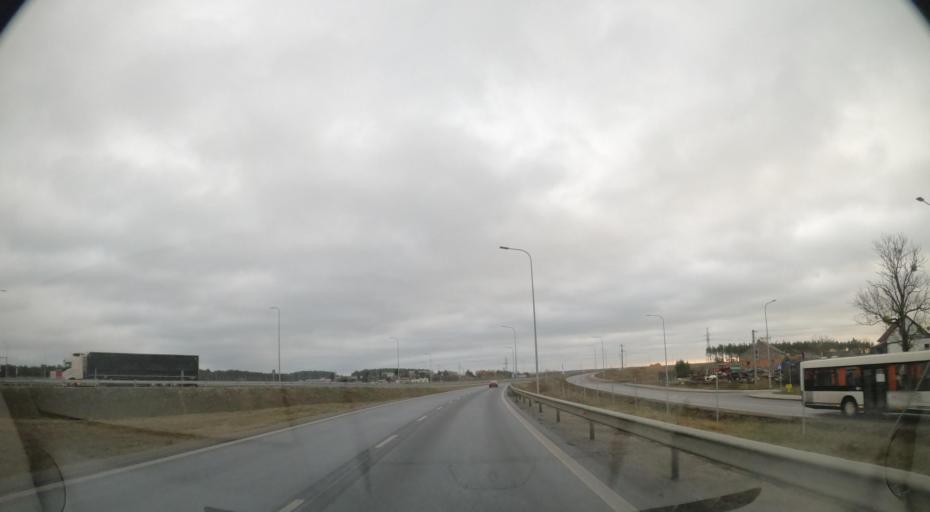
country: PL
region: Kujawsko-Pomorskie
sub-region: Powiat bydgoski
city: Biale Blota
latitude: 53.1561
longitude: 17.8827
